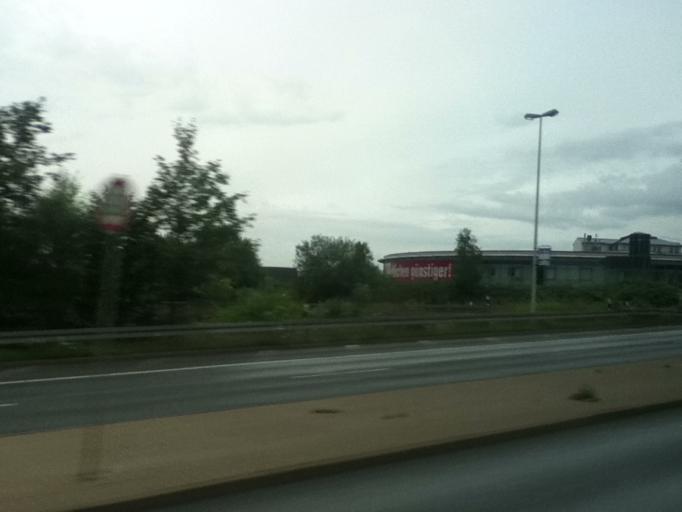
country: DE
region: Saxony
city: Wittgensdorf
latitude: 50.8589
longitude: 12.8688
